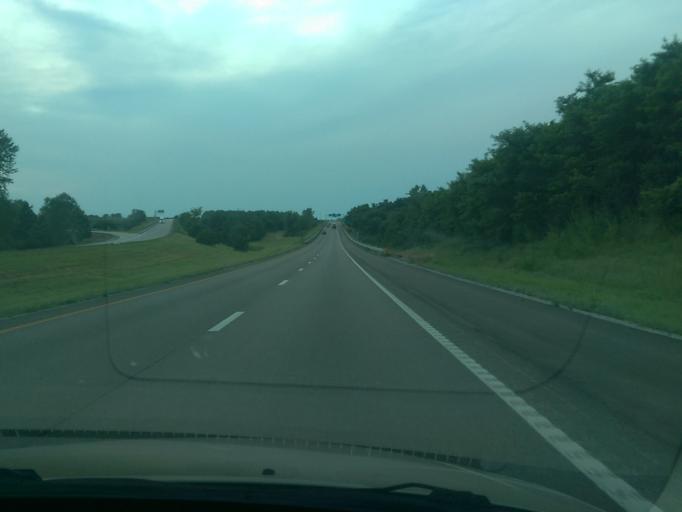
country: US
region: Missouri
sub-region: Andrew County
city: Country Club Village
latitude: 39.8812
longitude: -94.8479
